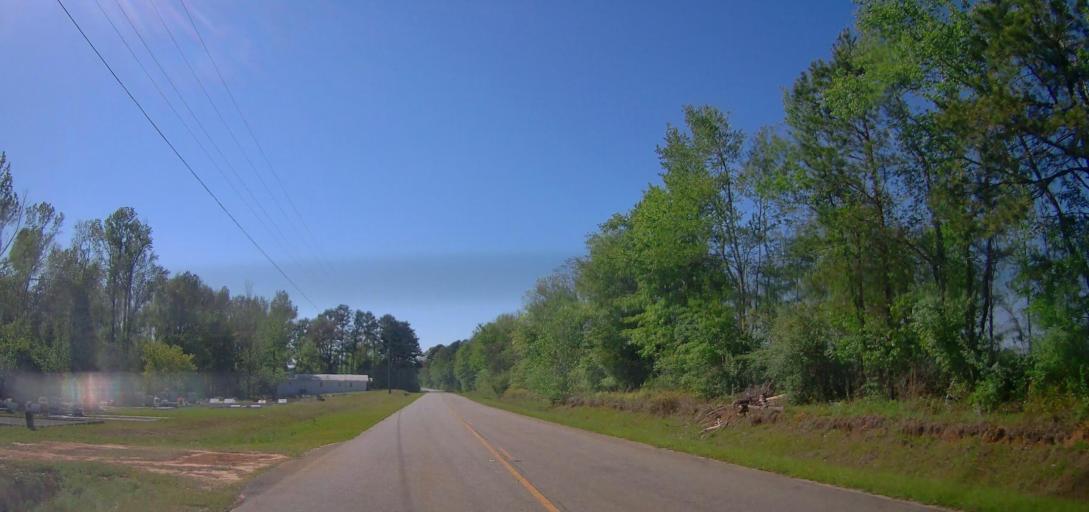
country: US
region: Georgia
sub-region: Pulaski County
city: Hawkinsville
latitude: 32.2420
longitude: -83.5642
